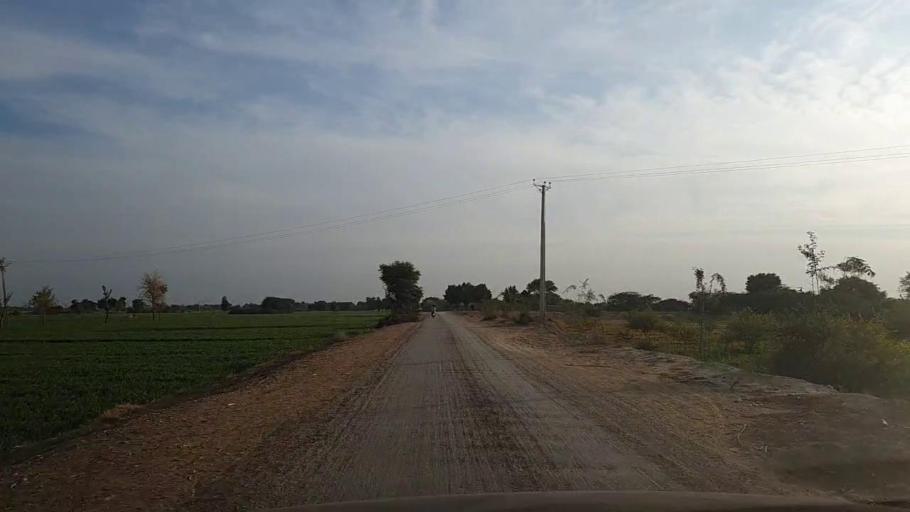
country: PK
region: Sindh
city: Jam Sahib
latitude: 26.4339
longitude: 68.5715
